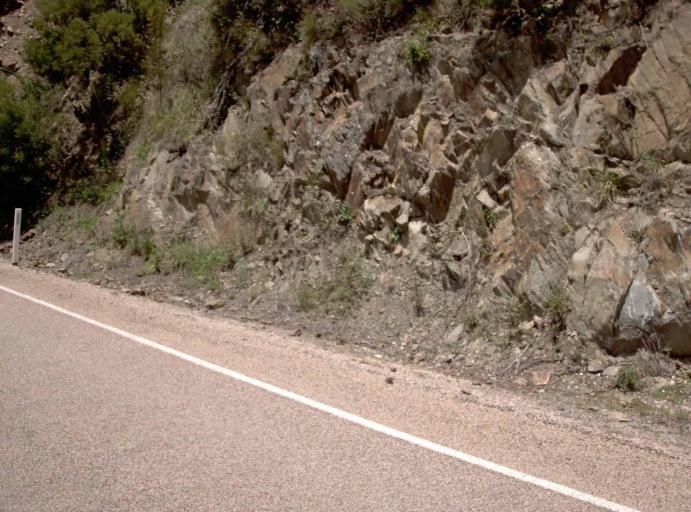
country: AU
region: Victoria
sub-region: East Gippsland
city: Lakes Entrance
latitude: -37.5525
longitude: 147.8697
